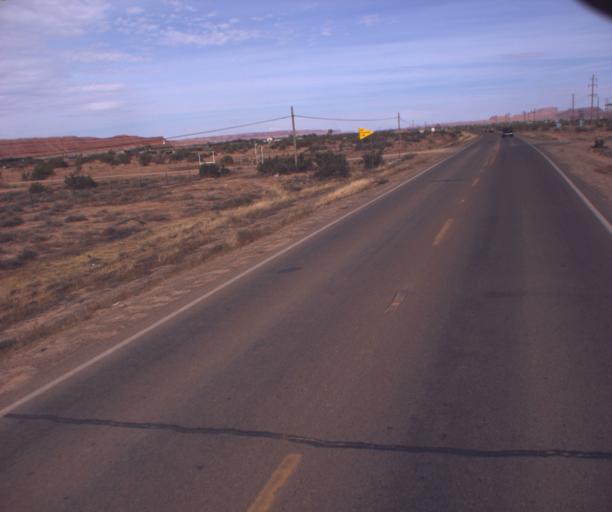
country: US
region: Arizona
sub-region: Apache County
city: Many Farms
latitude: 36.3594
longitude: -109.6153
